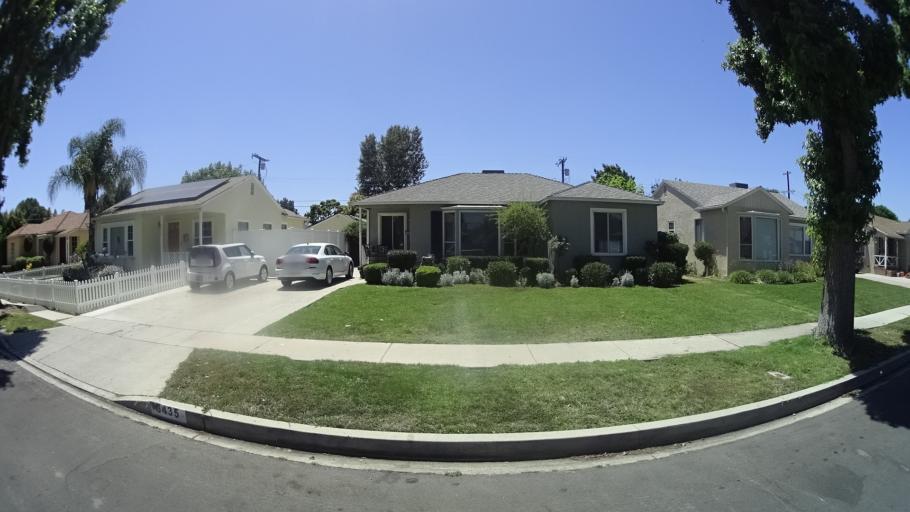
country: US
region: California
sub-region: Los Angeles County
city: Northridge
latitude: 34.1880
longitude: -118.5197
